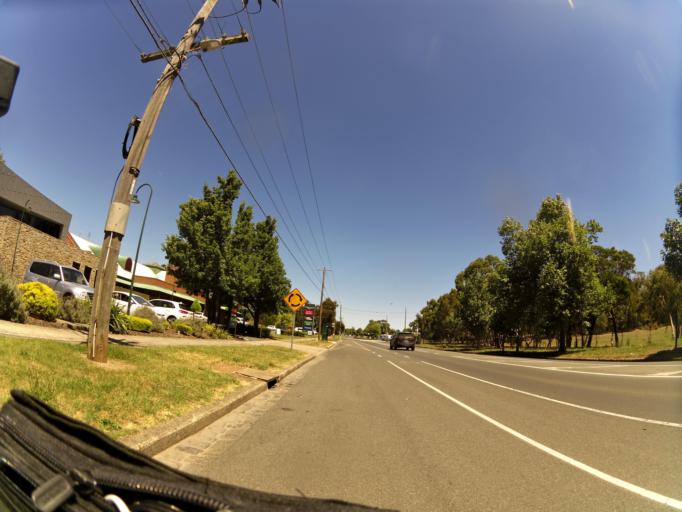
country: AU
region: Victoria
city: Mount Pleasant
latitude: -37.5812
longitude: 143.8681
